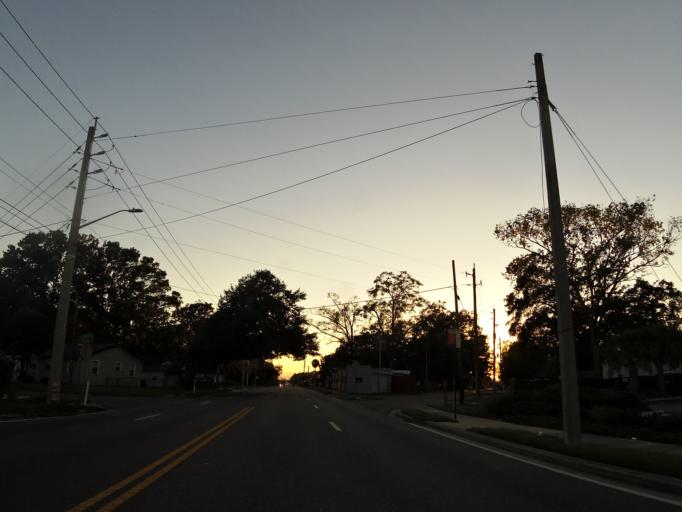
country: US
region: Florida
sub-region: Duval County
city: Jacksonville
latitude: 30.3173
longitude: -81.7263
